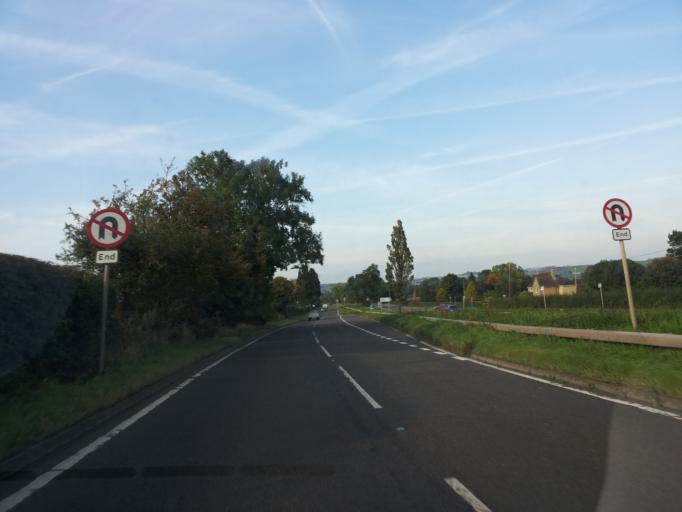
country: GB
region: England
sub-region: Staffordshire
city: Stone
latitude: 52.8708
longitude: -2.1306
